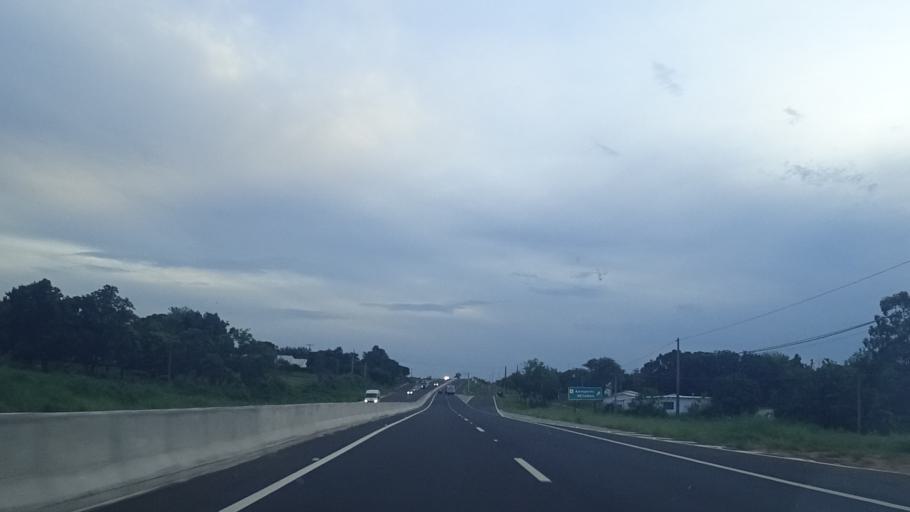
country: BR
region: Sao Paulo
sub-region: Presidente Prudente
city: Presidente Prudente
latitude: -22.1822
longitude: -51.4218
